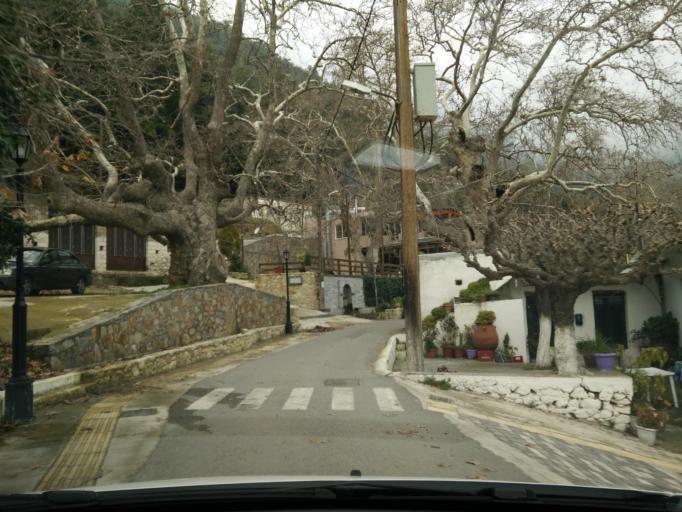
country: GR
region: Crete
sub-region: Nomos Lasithiou
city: Kritsa
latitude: 35.0468
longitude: 25.4891
